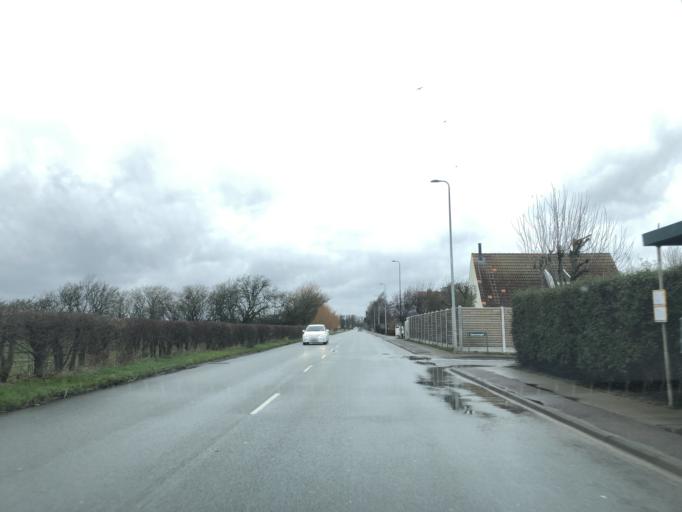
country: DK
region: Capital Region
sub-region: Dragor Kommune
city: Dragor
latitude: 55.5858
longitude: 12.6360
